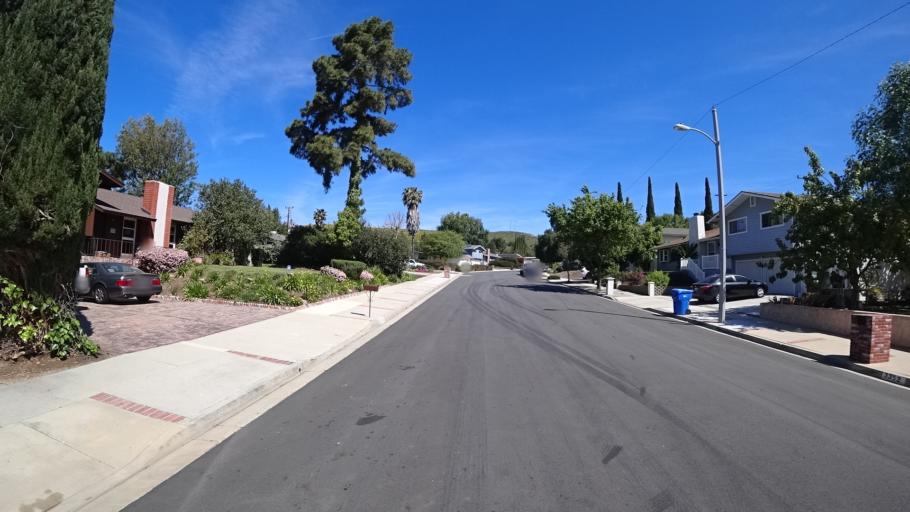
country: US
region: California
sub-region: Ventura County
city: Moorpark
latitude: 34.2272
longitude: -118.8668
